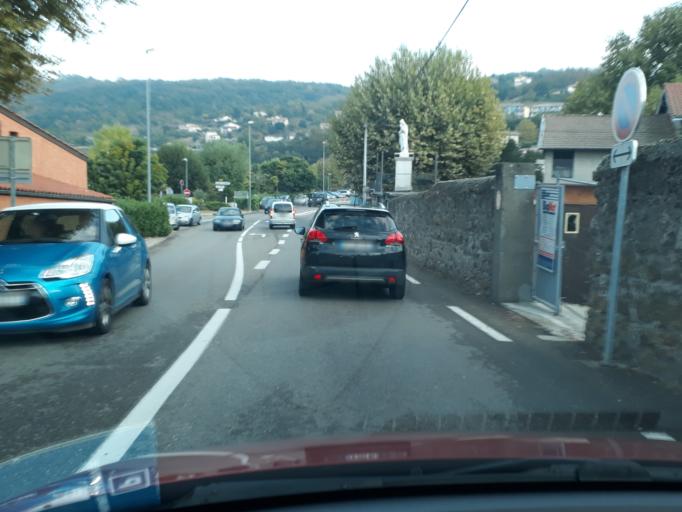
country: FR
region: Rhone-Alpes
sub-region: Departement de l'Isere
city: Les Roches-de-Condrieu
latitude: 45.4548
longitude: 4.7712
